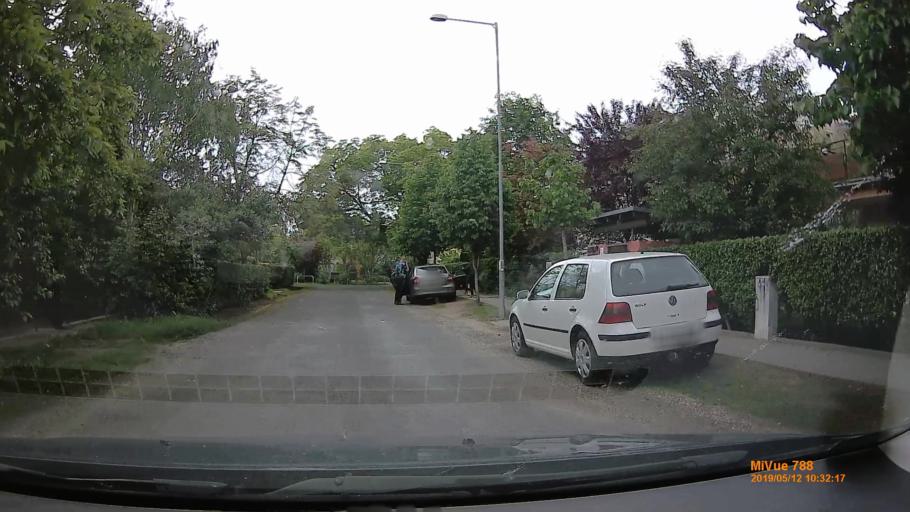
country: HU
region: Budapest
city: Budapest XVII. keruelet
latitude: 47.4812
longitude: 19.2249
